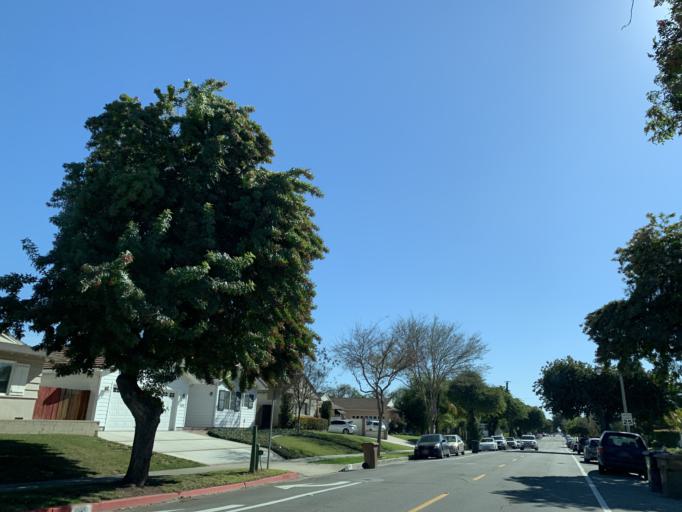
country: US
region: California
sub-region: Orange County
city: Fullerton
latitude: 33.8813
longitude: -117.8985
